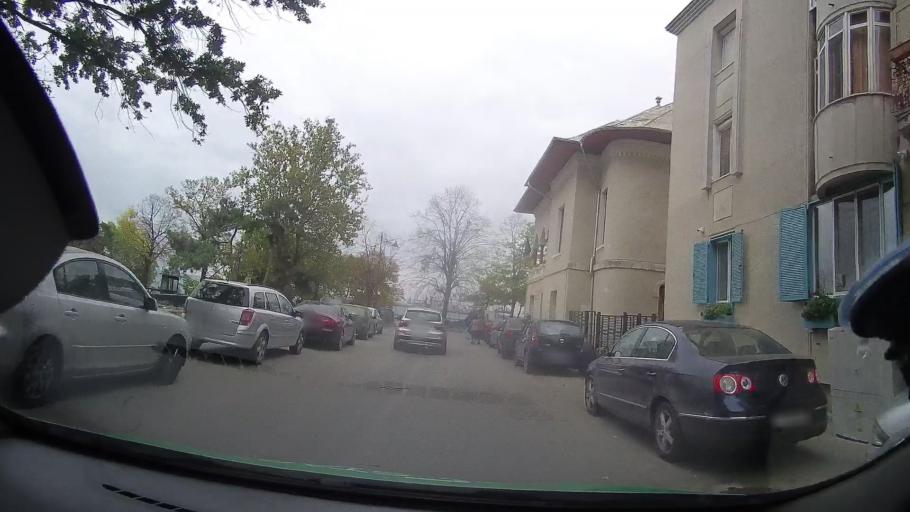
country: RO
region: Constanta
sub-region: Municipiul Constanta
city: Constanta
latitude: 44.1712
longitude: 28.6606
